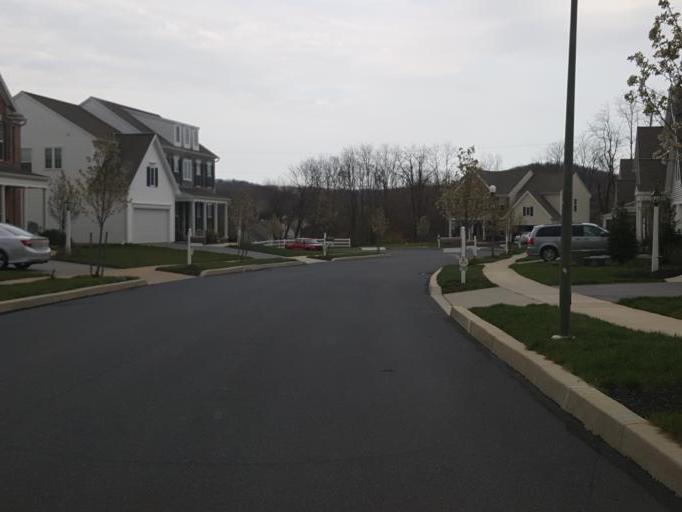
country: US
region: Pennsylvania
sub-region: Dauphin County
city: Hummelstown
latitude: 40.2402
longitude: -76.7204
